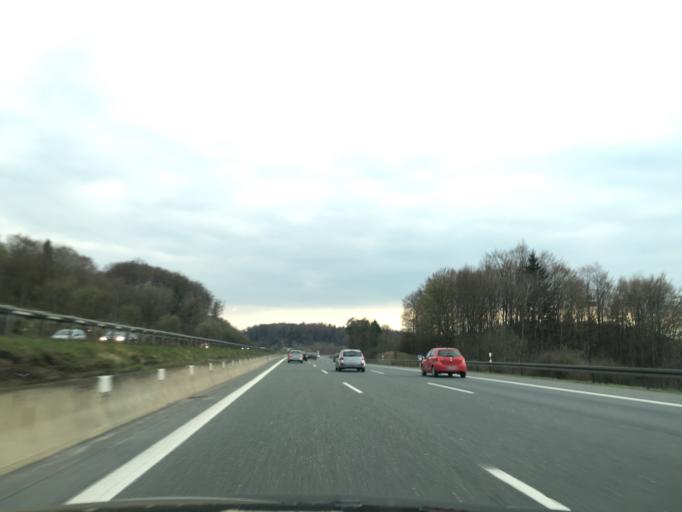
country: DE
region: Bavaria
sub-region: Regierungsbezirk Mittelfranken
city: Simmelsdorf
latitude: 49.6052
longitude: 11.3668
